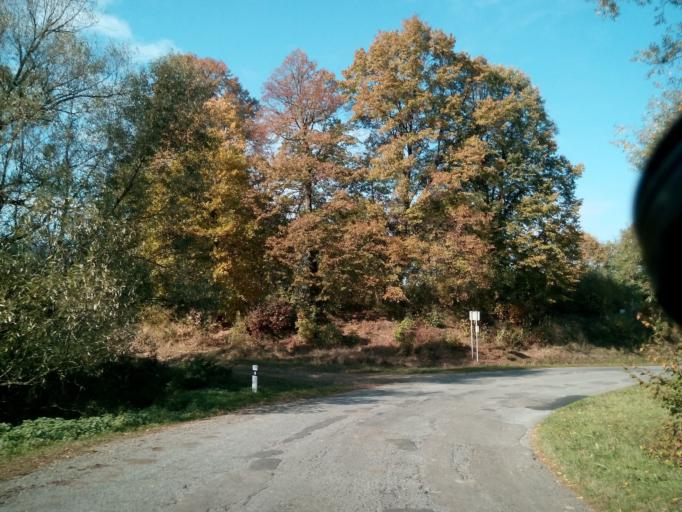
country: SK
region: Presovsky
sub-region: Okres Bardejov
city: Bardejov
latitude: 49.3433
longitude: 21.3863
